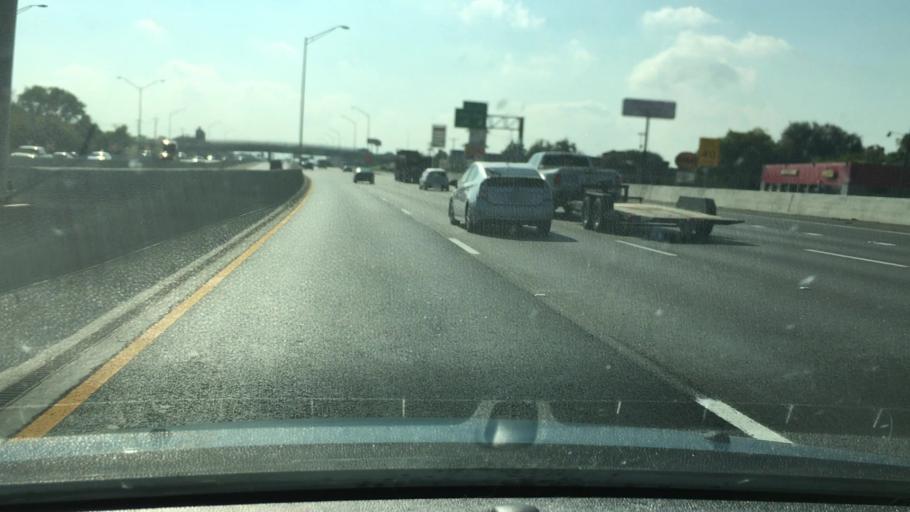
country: US
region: Texas
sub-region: Denton County
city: Lewisville
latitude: 33.0413
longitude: -97.0055
